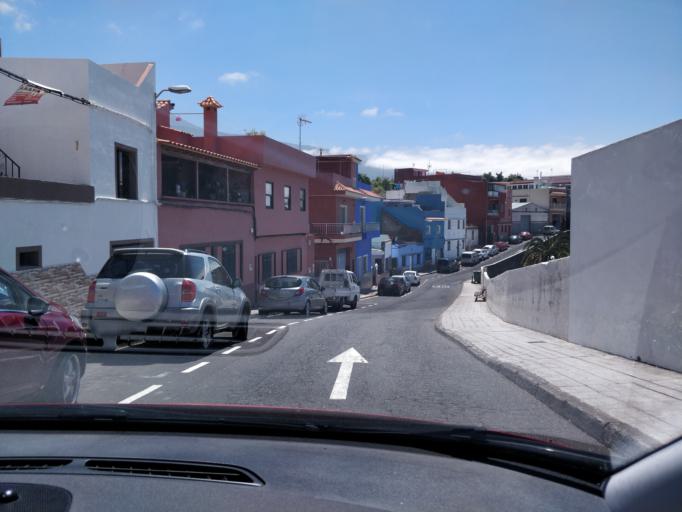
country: ES
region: Canary Islands
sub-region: Provincia de Santa Cruz de Tenerife
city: La Orotava
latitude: 28.3847
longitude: -16.5191
